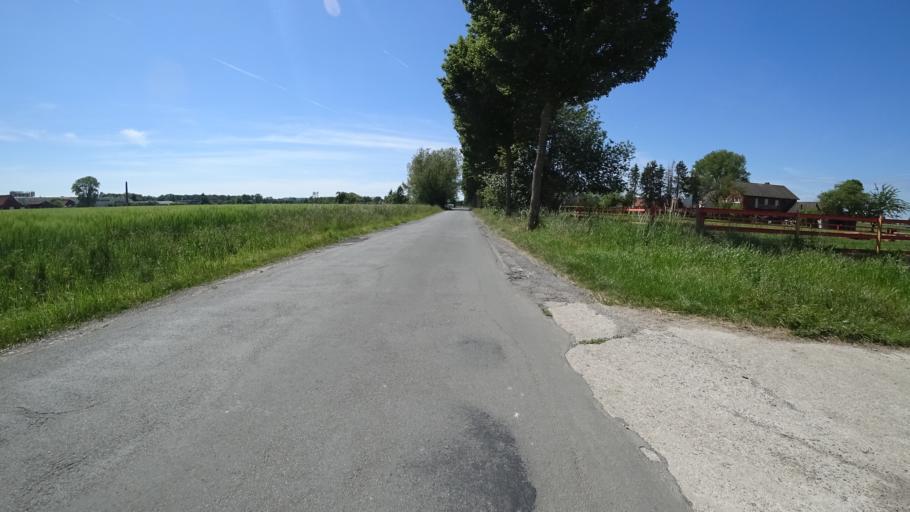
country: DE
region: North Rhine-Westphalia
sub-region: Regierungsbezirk Detmold
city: Rheda-Wiedenbruck
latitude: 51.8203
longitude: 8.2981
